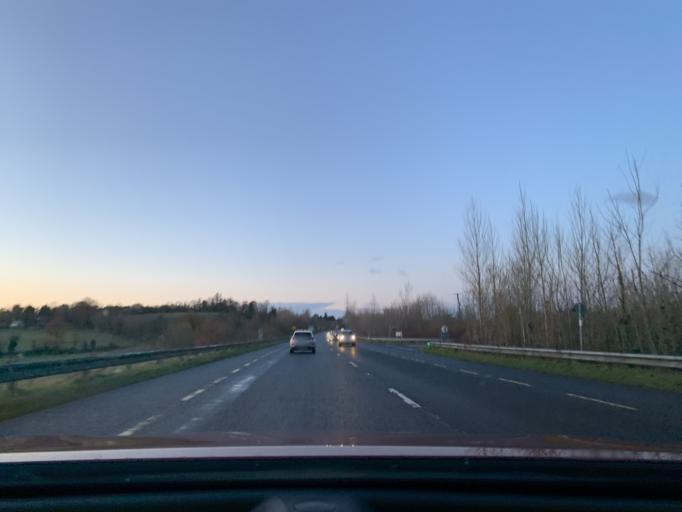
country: IE
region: Connaught
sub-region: County Leitrim
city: Carrick-on-Shannon
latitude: 53.9240
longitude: -7.9942
